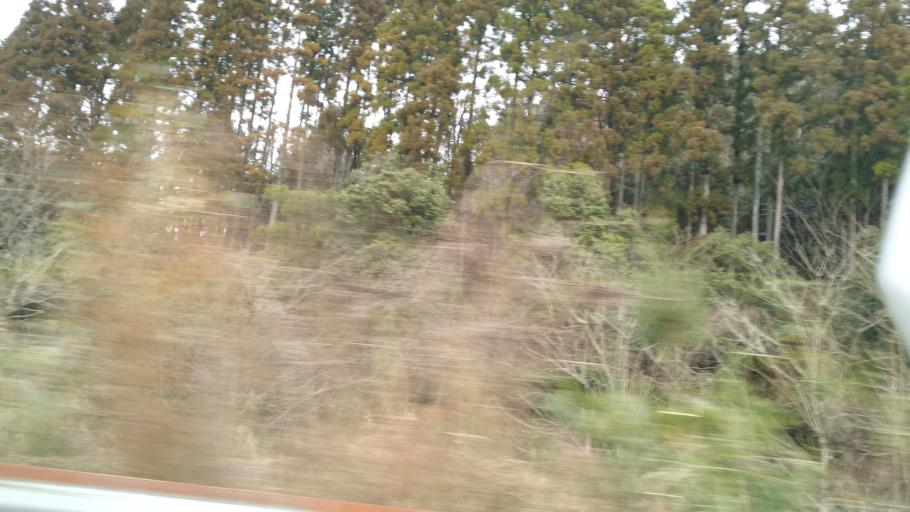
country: JP
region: Kyoto
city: Ayabe
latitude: 35.3178
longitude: 135.3631
